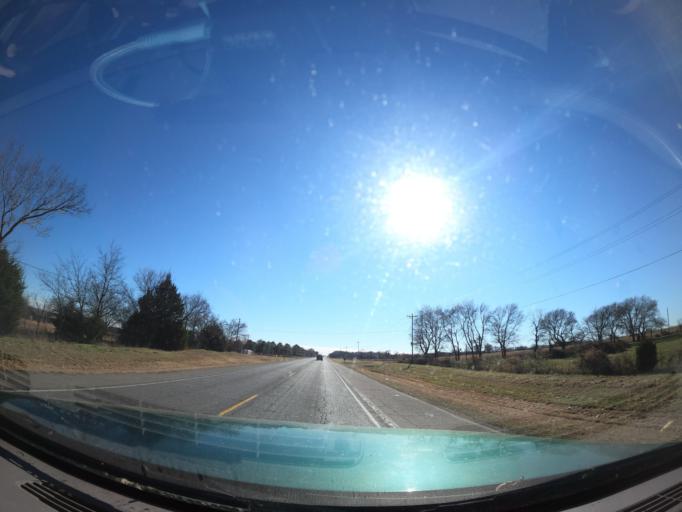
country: US
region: Oklahoma
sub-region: Muskogee County
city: Haskell
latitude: 35.8499
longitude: -95.6775
